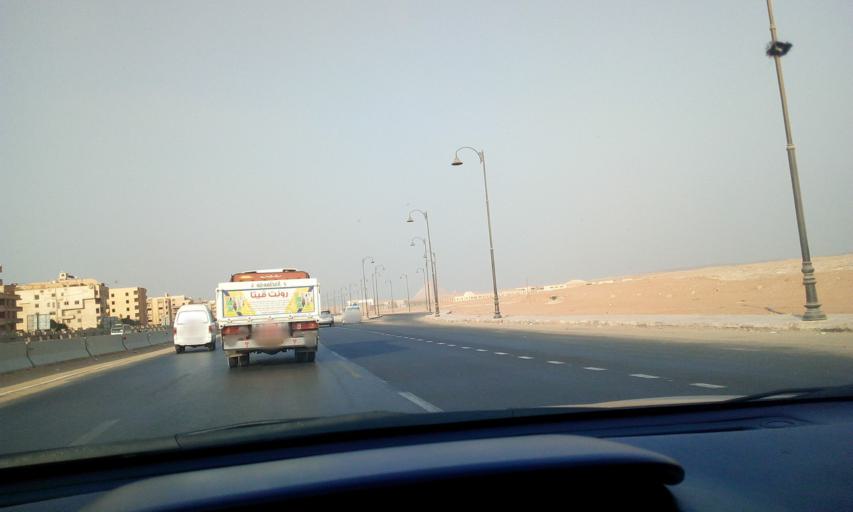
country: EG
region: Al Jizah
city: Al Jizah
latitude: 29.9534
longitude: 31.1041
